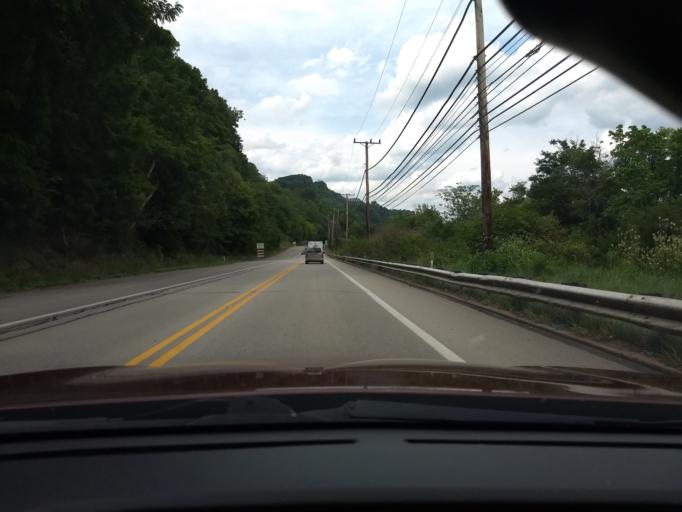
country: US
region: Pennsylvania
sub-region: Allegheny County
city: Verona
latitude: 40.5123
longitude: -79.8525
